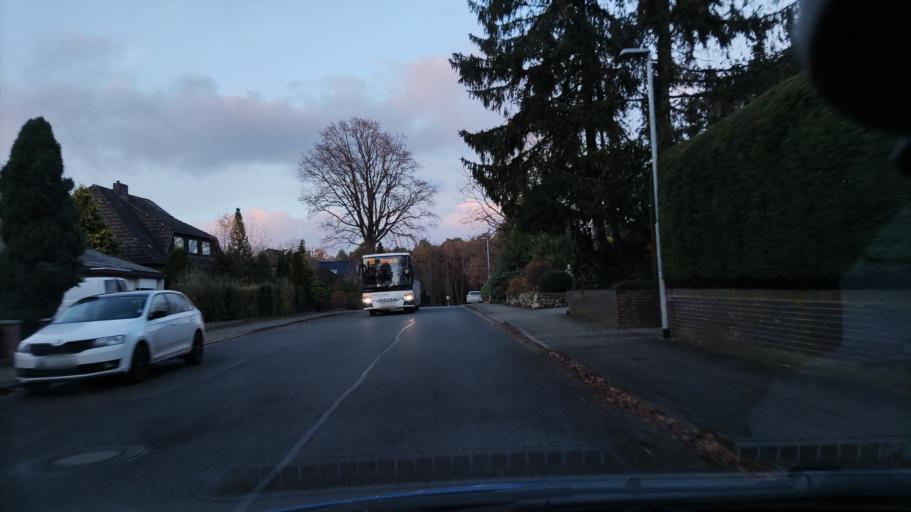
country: DE
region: Lower Saxony
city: Schneverdingen
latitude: 53.1164
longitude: 9.8019
